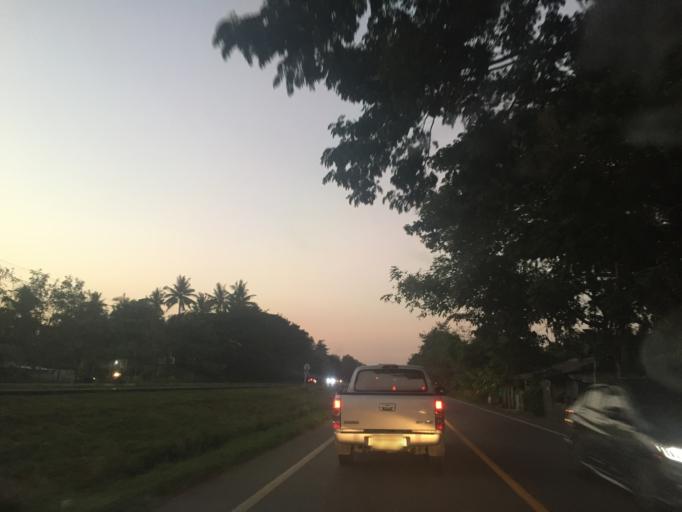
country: TH
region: Chiang Mai
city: Saraphi
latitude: 18.7057
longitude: 99.0439
